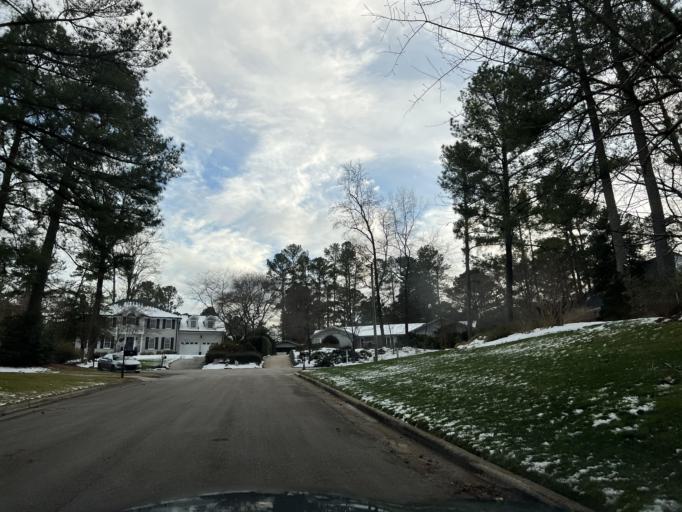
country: US
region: North Carolina
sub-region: Wake County
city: West Raleigh
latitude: 35.8746
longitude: -78.6029
